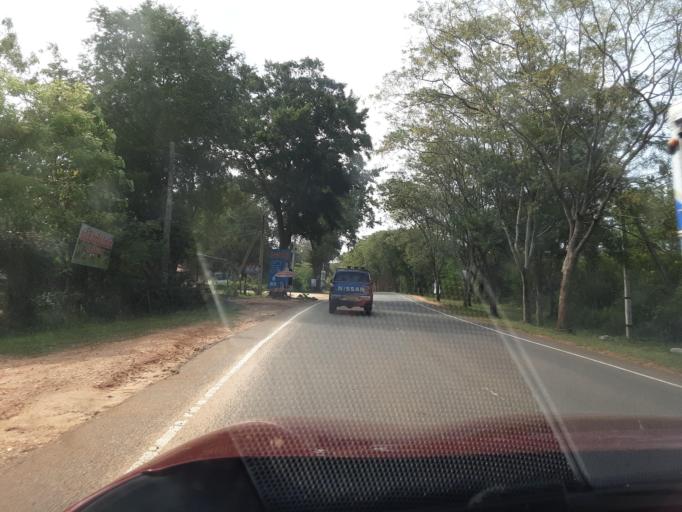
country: LK
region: Uva
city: Haputale
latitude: 6.3628
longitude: 81.1793
